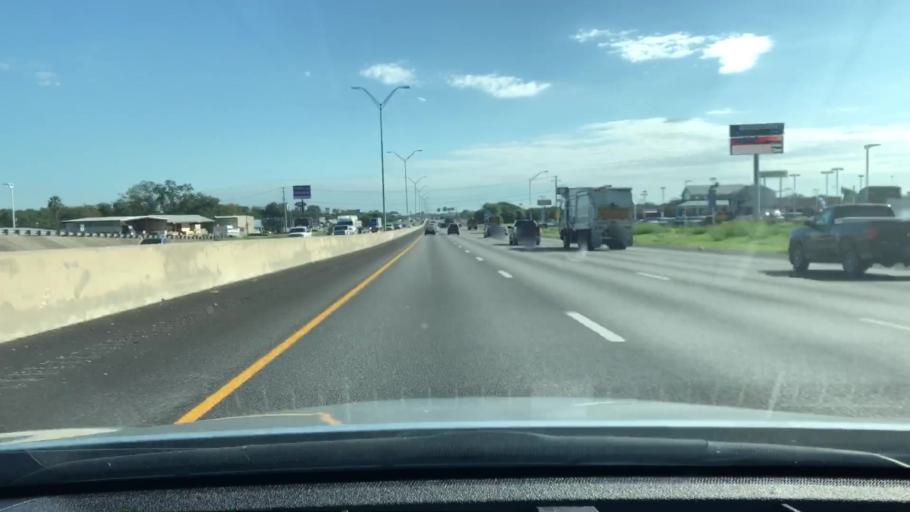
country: US
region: Texas
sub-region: Comal County
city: New Braunfels
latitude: 29.6892
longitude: -98.1165
